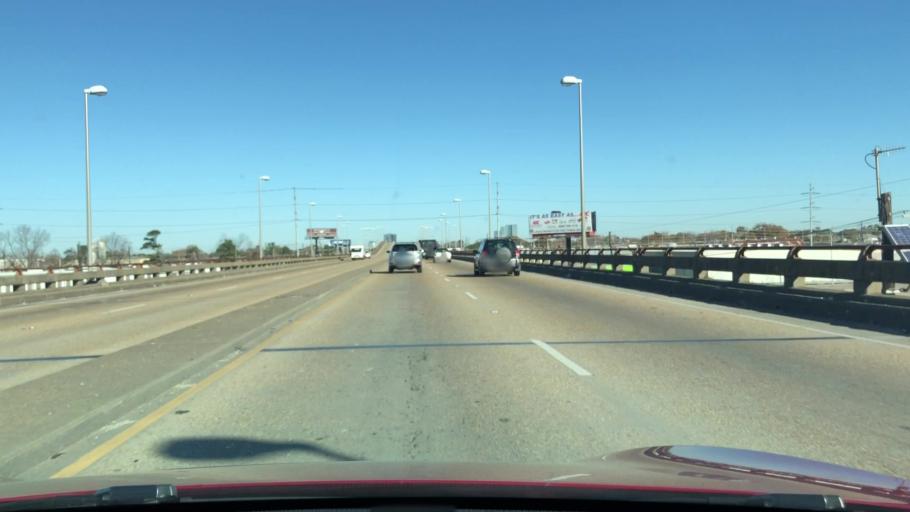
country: US
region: Louisiana
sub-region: Jefferson Parish
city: Jefferson
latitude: 29.9704
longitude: -90.1565
